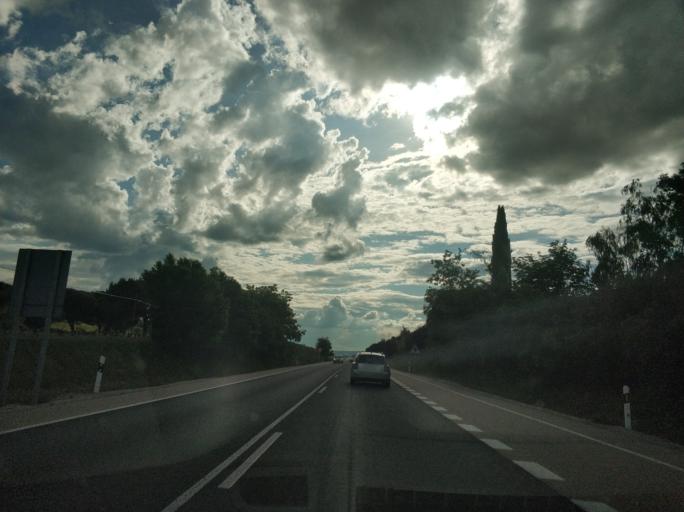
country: ES
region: Castille and Leon
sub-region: Provincia de Valladolid
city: Valbuena de Duero
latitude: 41.6286
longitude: -4.2943
